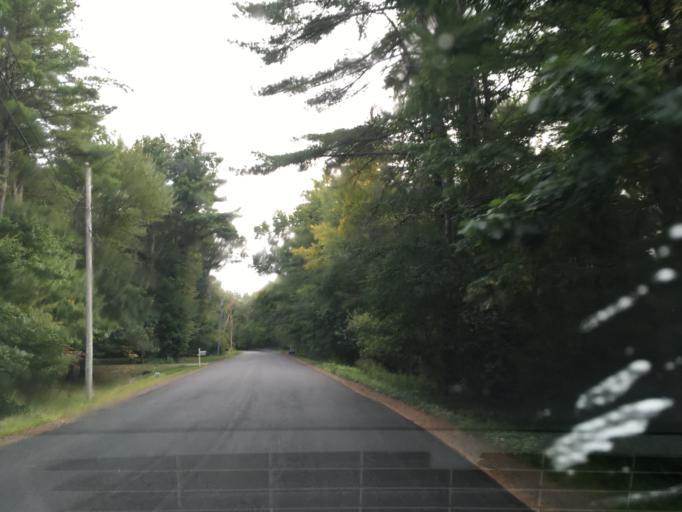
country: US
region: New Hampshire
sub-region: Rockingham County
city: Stratham Station
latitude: 43.0126
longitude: -70.8886
